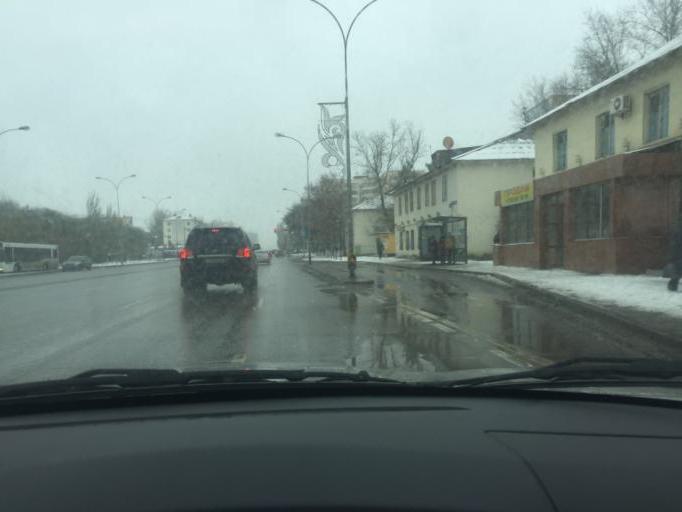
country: KZ
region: Astana Qalasy
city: Astana
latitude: 51.1741
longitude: 71.4117
